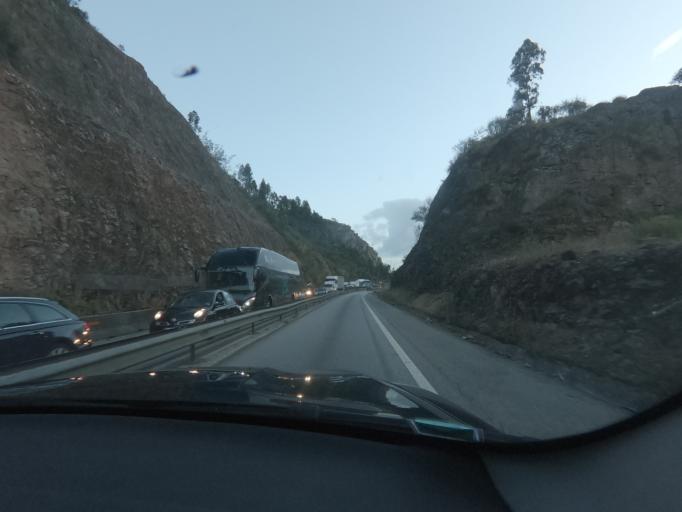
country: PT
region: Coimbra
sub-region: Penacova
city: Penacova
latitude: 40.2841
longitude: -8.2633
